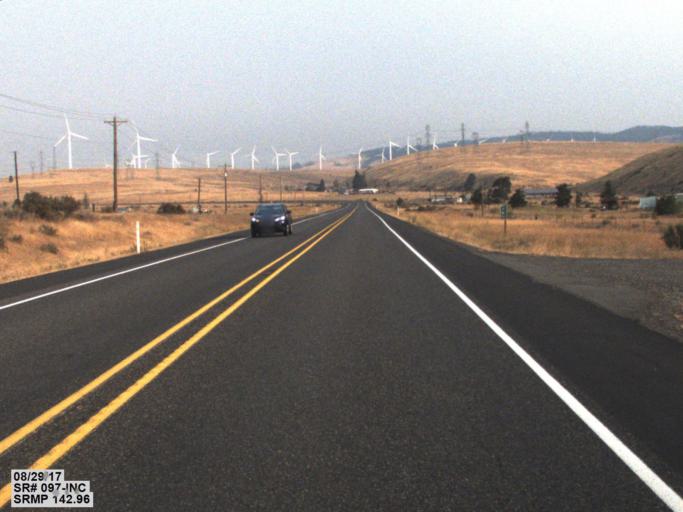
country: US
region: Washington
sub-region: Kittitas County
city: Ellensburg
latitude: 47.1154
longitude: -120.6669
